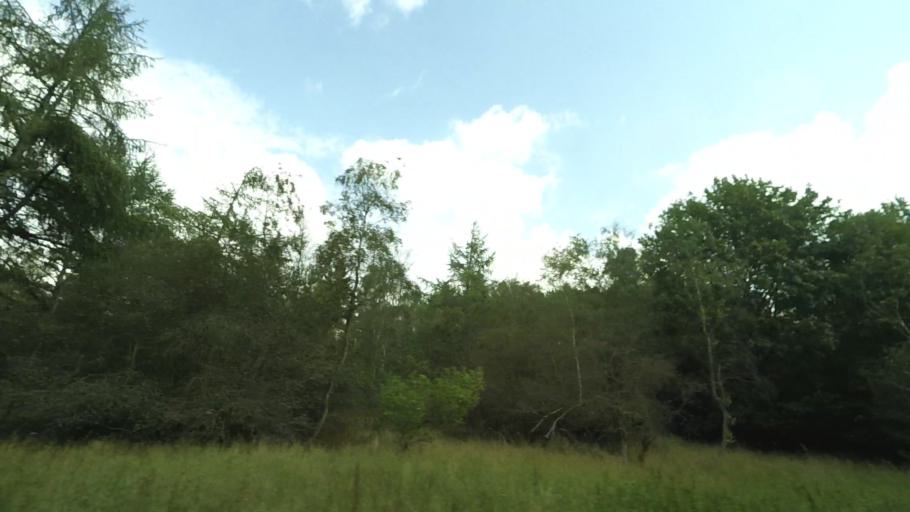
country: DK
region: Central Jutland
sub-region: Norddjurs Kommune
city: Auning
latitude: 56.5104
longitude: 10.4173
